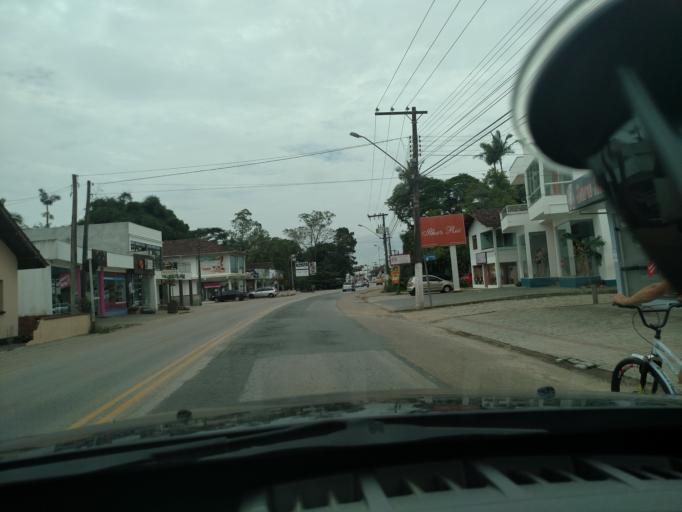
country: BR
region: Santa Catarina
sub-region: Gaspar
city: Gaspar
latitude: -26.9041
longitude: -48.8366
